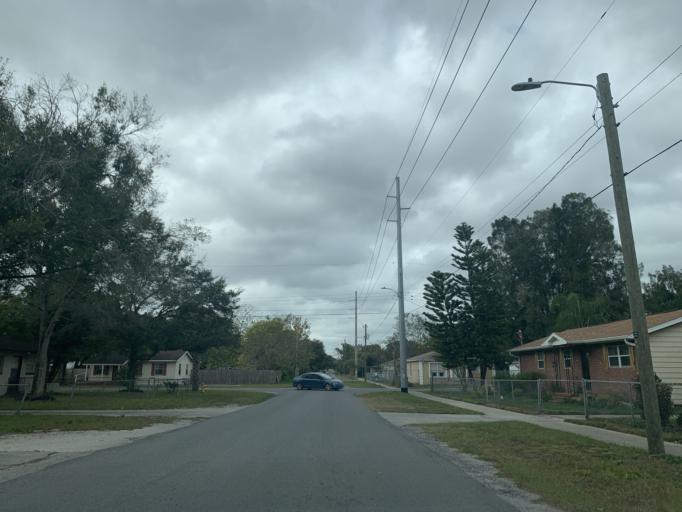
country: US
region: Florida
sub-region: Hillsborough County
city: East Lake-Orient Park
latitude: 27.9778
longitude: -82.3964
